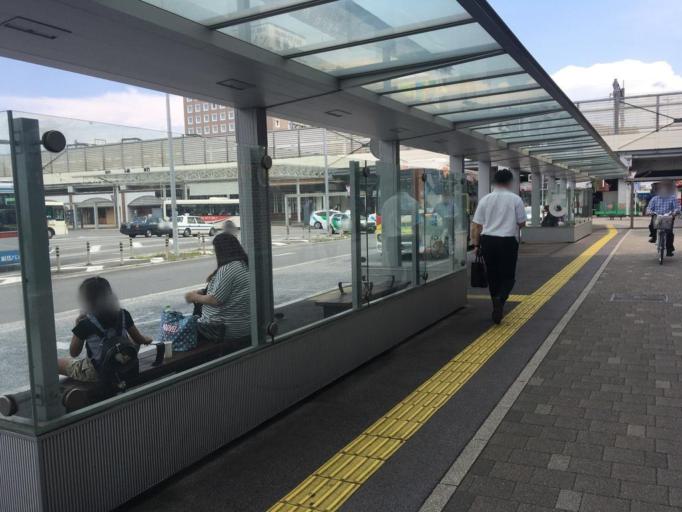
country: JP
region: Gunma
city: Maebashi-shi
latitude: 36.3839
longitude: 139.0721
